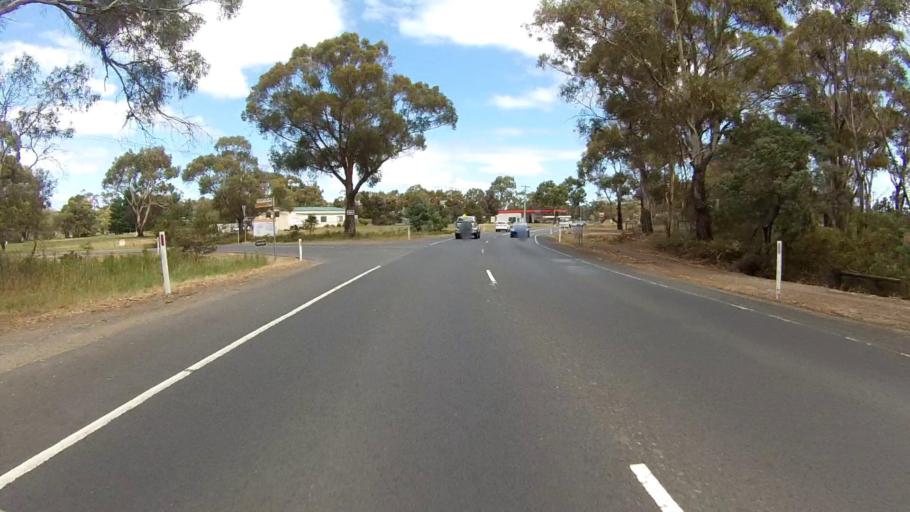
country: AU
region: Tasmania
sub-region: Sorell
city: Sorell
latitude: -42.8472
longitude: 147.6274
